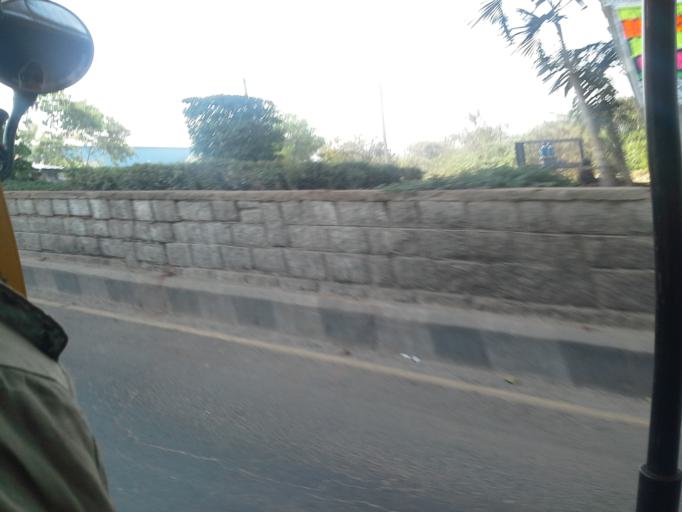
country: IN
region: Telangana
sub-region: Hyderabad
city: Hyderabad
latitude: 17.3716
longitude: 78.4294
